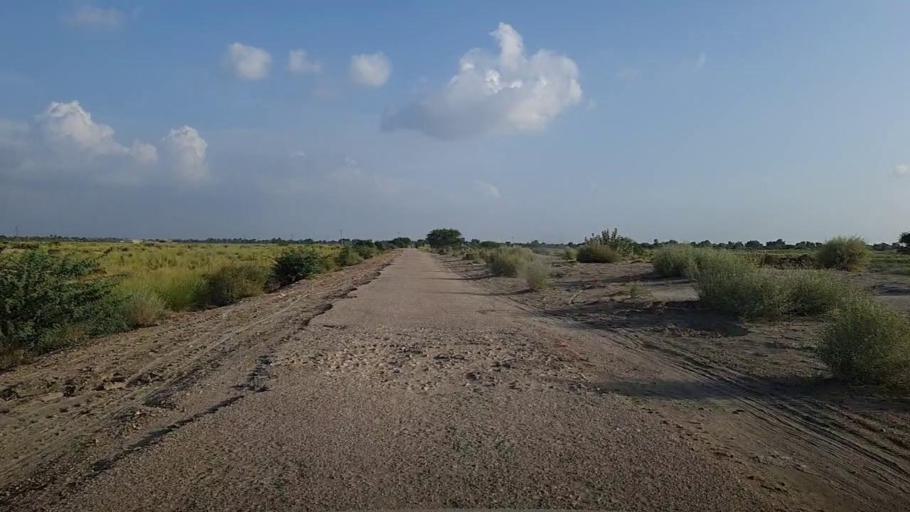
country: PK
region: Sindh
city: Hingorja
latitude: 27.0785
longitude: 68.4188
